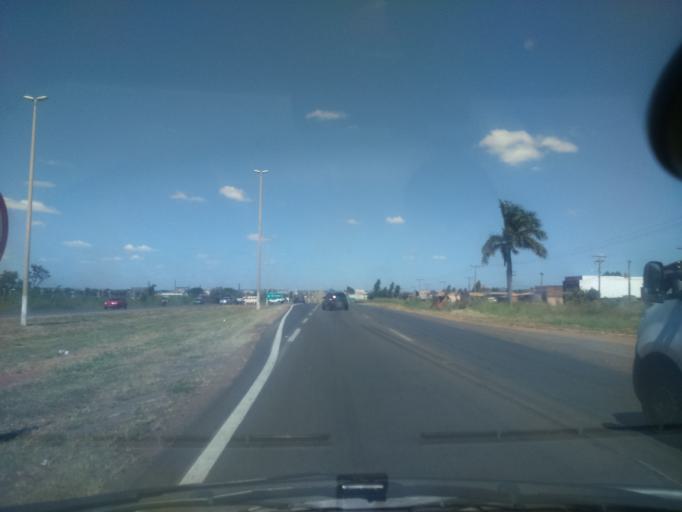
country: BR
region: Goias
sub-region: Luziania
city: Luziania
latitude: -16.1138
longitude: -47.9692
